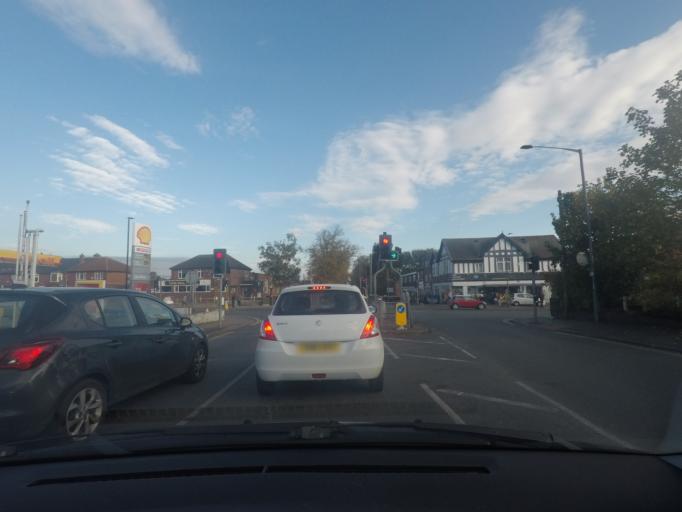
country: GB
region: England
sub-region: City of York
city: Heslington
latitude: 53.9539
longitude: -1.0591
